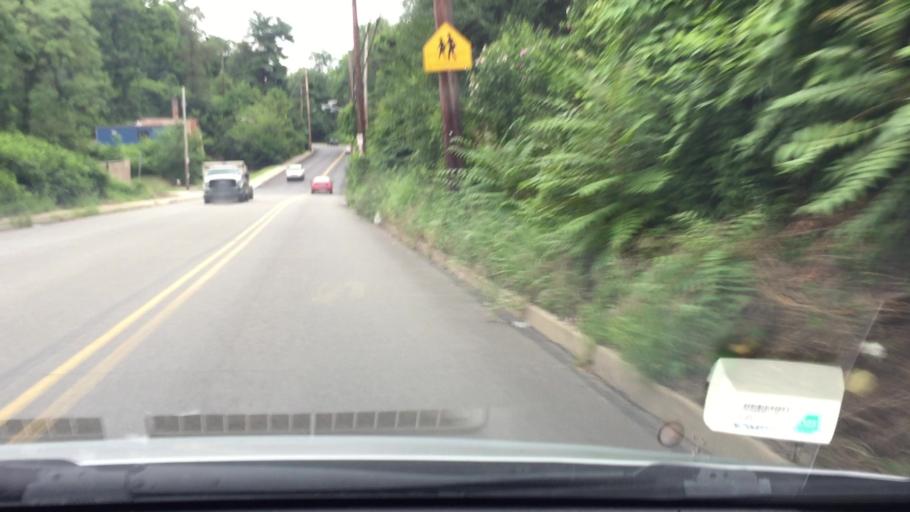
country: US
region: Pennsylvania
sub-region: Allegheny County
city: Pittsburgh
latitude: 40.4605
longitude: -80.0086
